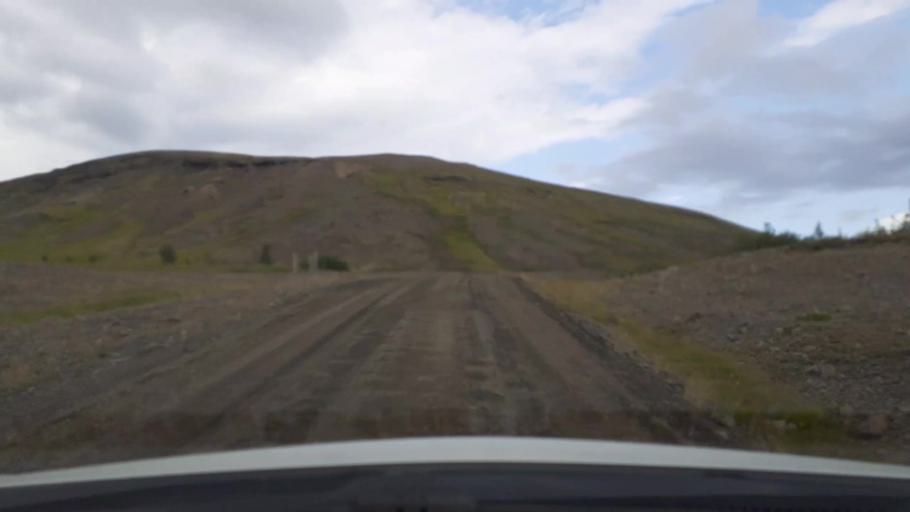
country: IS
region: Capital Region
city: Mosfellsbaer
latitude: 64.2950
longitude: -21.6617
